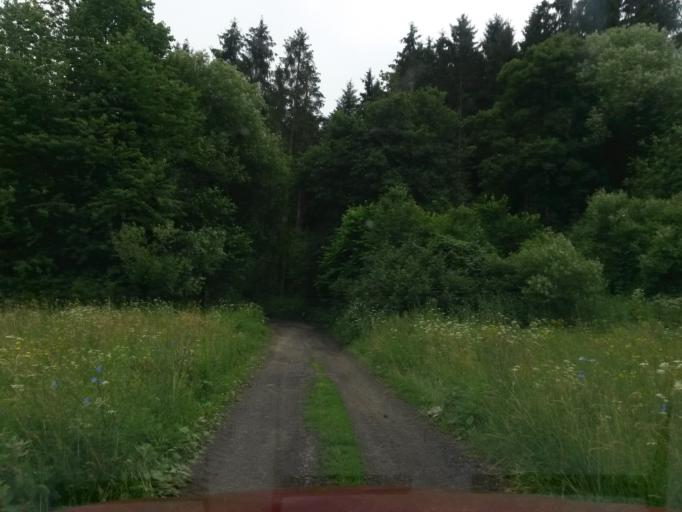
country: SK
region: Nitriansky
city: Handlova
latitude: 48.7373
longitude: 18.7478
